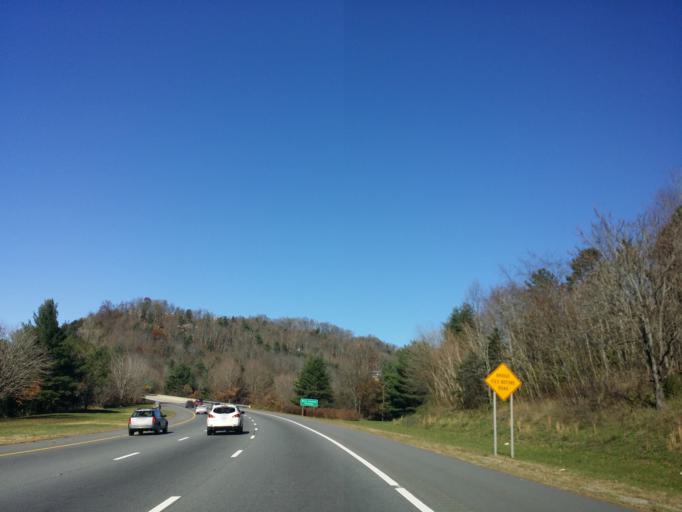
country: US
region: North Carolina
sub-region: Buncombe County
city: Asheville
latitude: 35.5973
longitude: -82.5294
